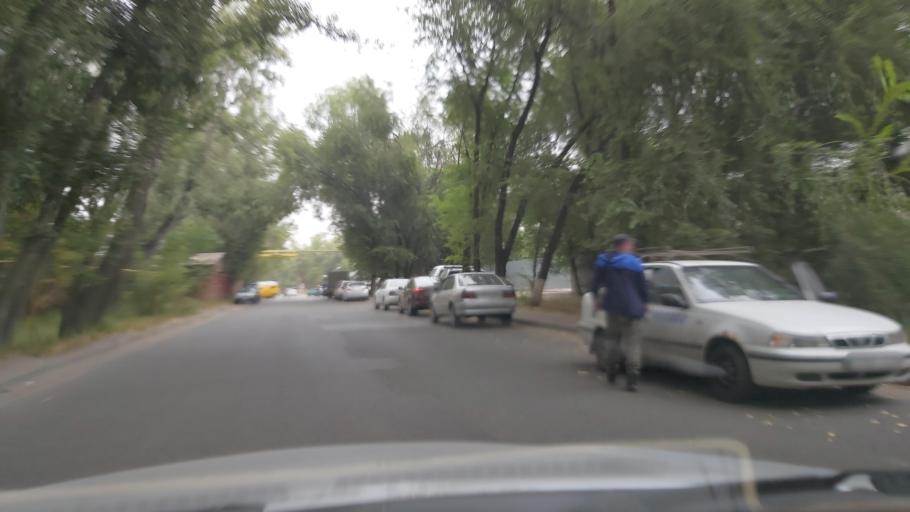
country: KZ
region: Almaty Oblysy
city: Pervomayskiy
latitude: 43.3487
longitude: 76.9732
